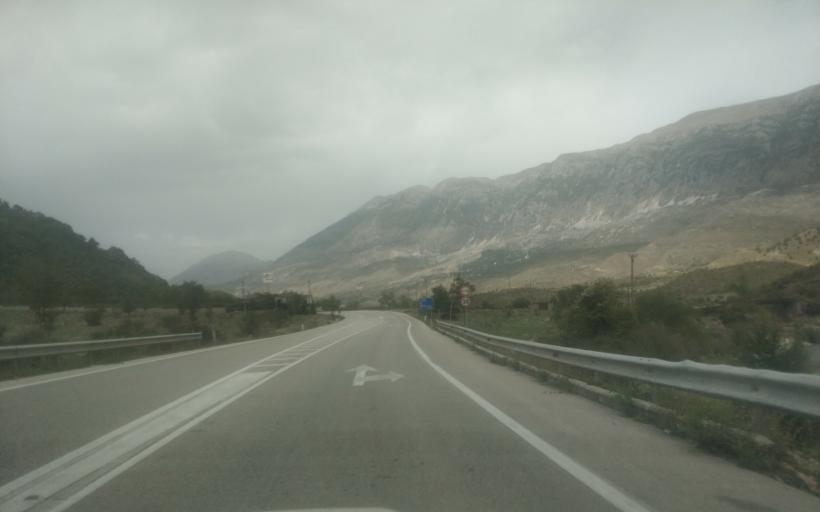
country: AL
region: Gjirokaster
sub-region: Rrethi i Gjirokastres
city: Picar
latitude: 40.2070
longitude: 20.0889
